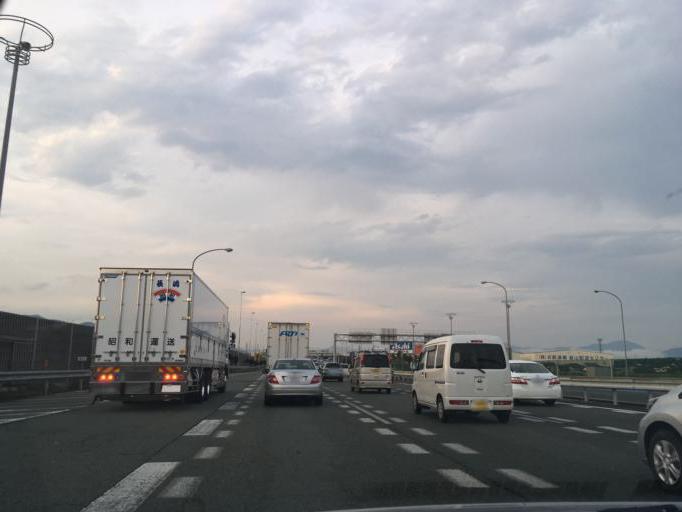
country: JP
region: Saga Prefecture
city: Tosu
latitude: 33.4018
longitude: 130.5382
